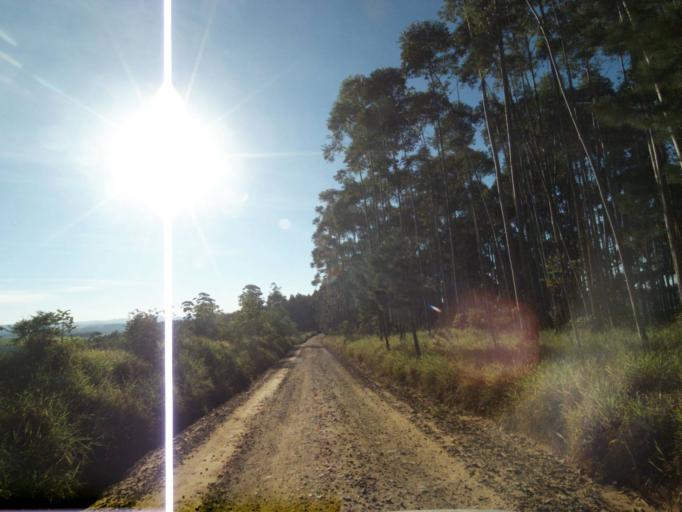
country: BR
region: Parana
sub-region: Tibagi
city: Tibagi
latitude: -24.5444
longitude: -50.6226
